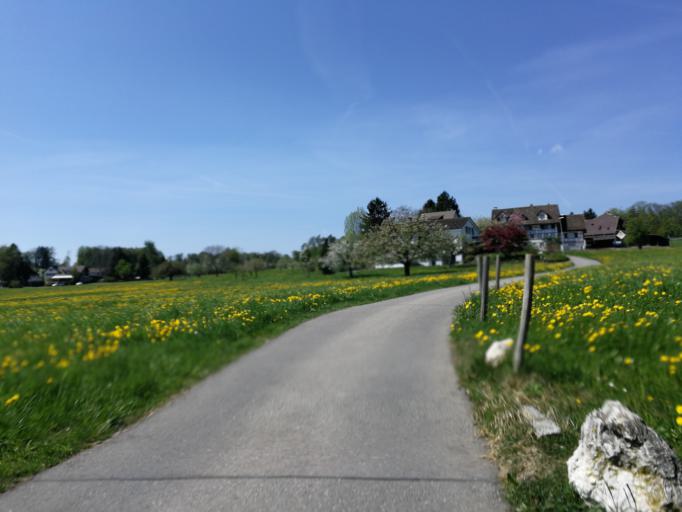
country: CH
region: Zurich
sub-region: Bezirk Meilen
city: Hombrechtikon
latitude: 47.2549
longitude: 8.7596
